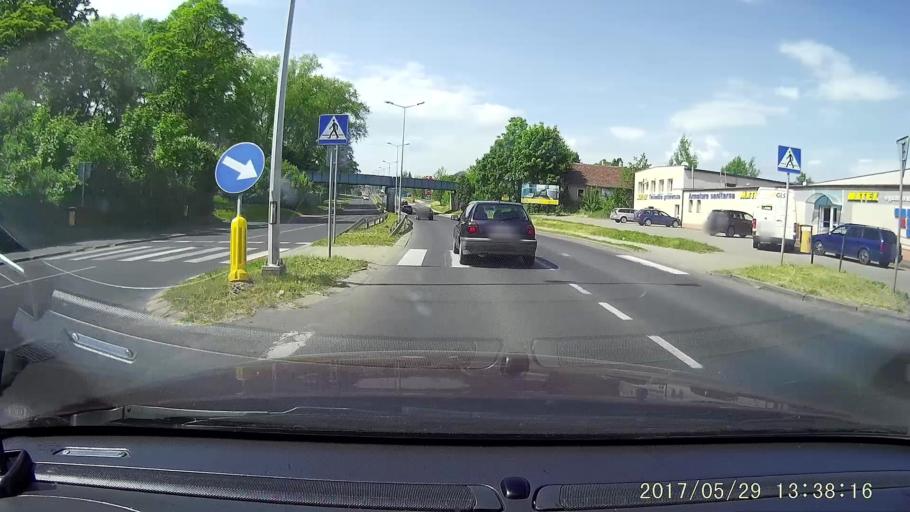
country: PL
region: Lower Silesian Voivodeship
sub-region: Powiat lubanski
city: Luban
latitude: 51.1218
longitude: 15.2949
